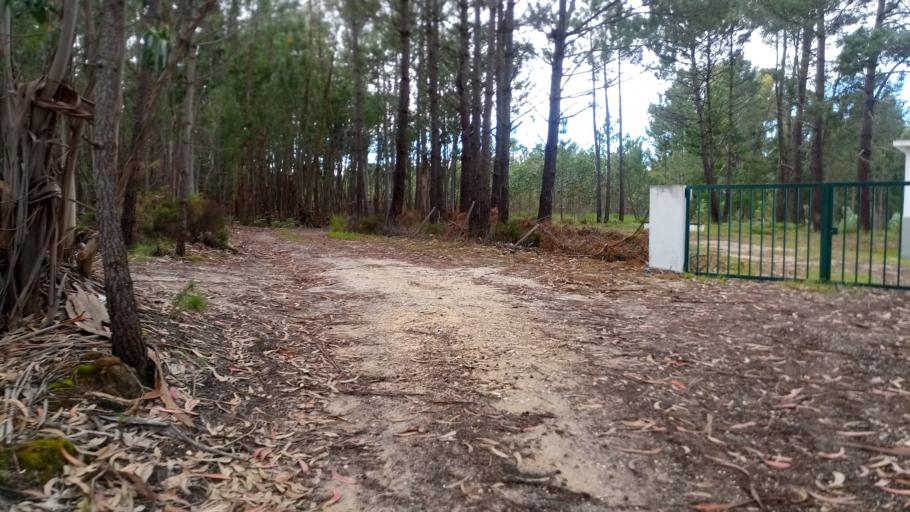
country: PT
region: Leiria
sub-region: Caldas da Rainha
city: Caldas da Rainha
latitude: 39.4463
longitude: -9.1658
